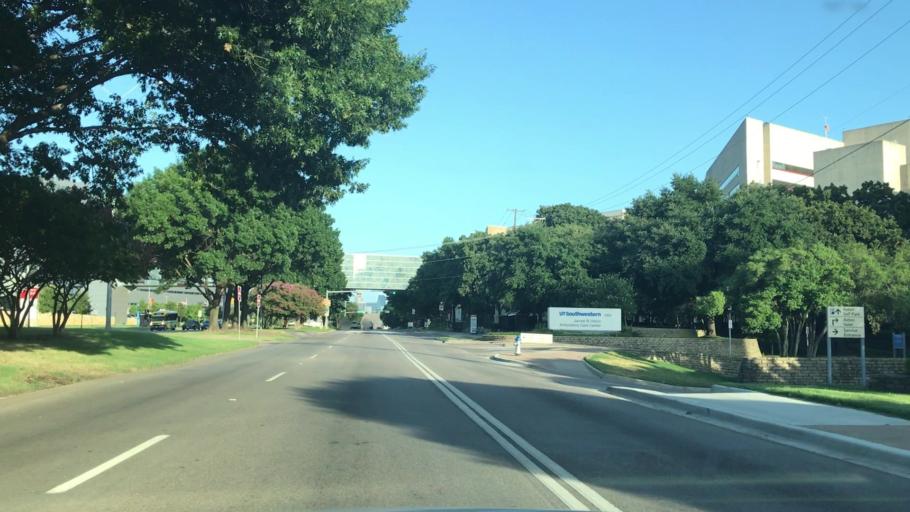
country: US
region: Texas
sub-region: Dallas County
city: Dallas
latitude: 32.8130
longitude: -96.8391
